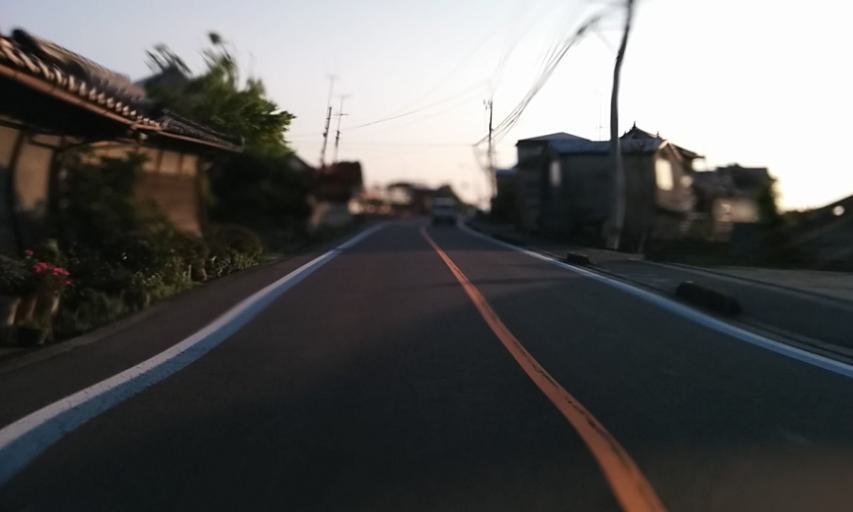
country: JP
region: Ehime
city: Masaki-cho
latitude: 33.7785
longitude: 132.7562
